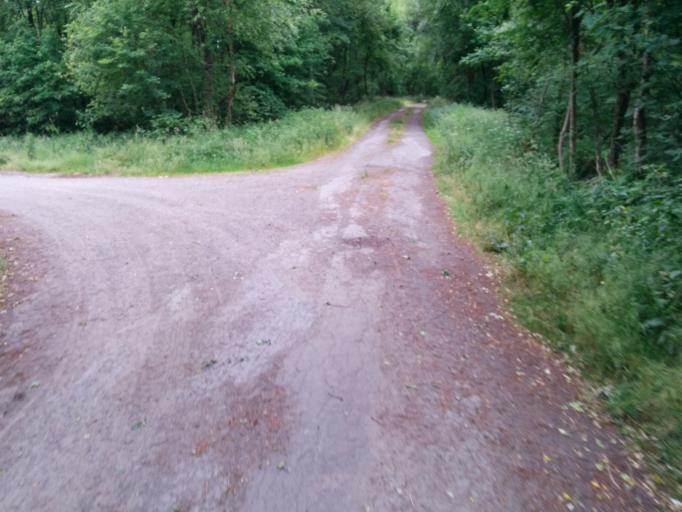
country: DE
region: Lower Saxony
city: Vechta
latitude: 52.7019
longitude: 8.3183
